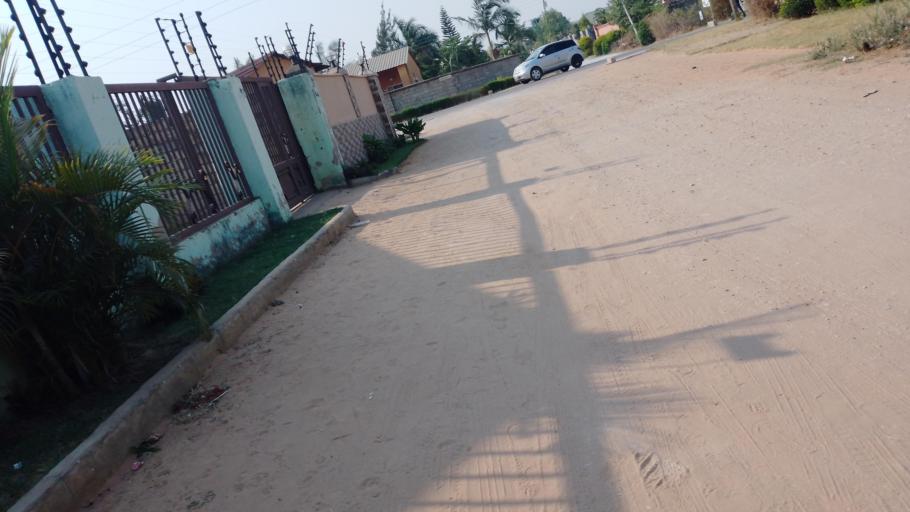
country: ZM
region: Lusaka
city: Lusaka
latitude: -15.3989
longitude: 28.3858
